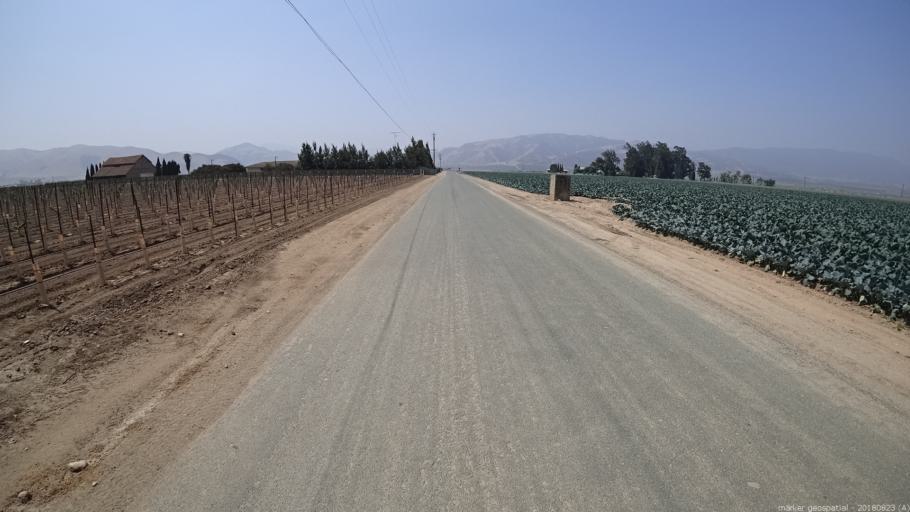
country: US
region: California
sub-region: Monterey County
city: Greenfield
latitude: 36.3201
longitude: -121.2785
